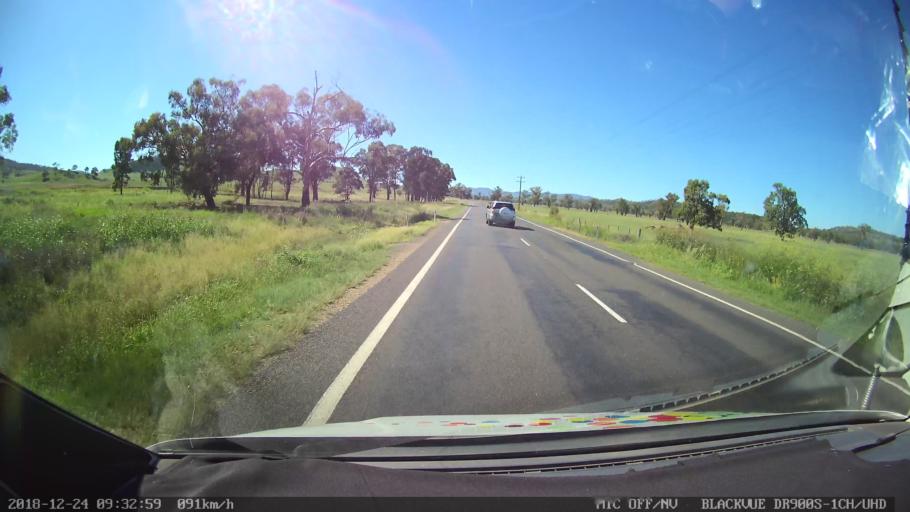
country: AU
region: New South Wales
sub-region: Liverpool Plains
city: Quirindi
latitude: -31.5978
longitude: 150.7048
